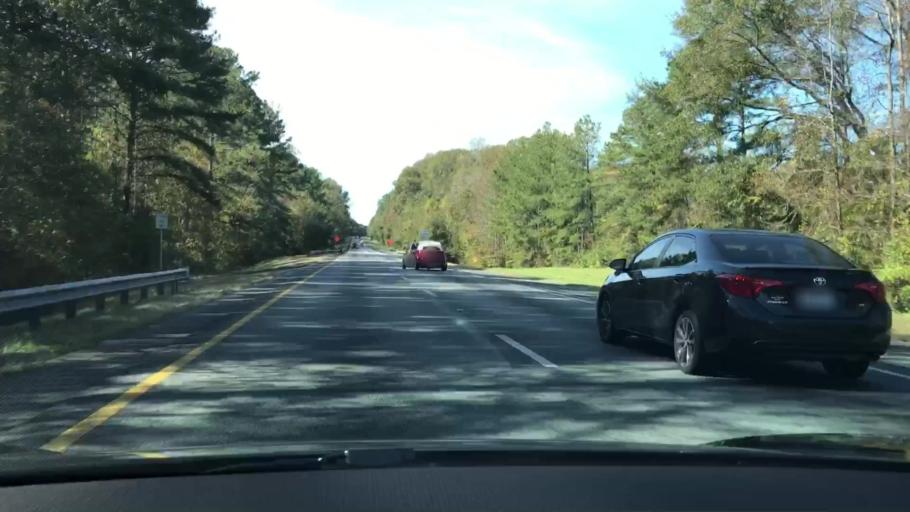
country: US
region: Georgia
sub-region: Morgan County
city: Madison
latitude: 33.5775
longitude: -83.5494
